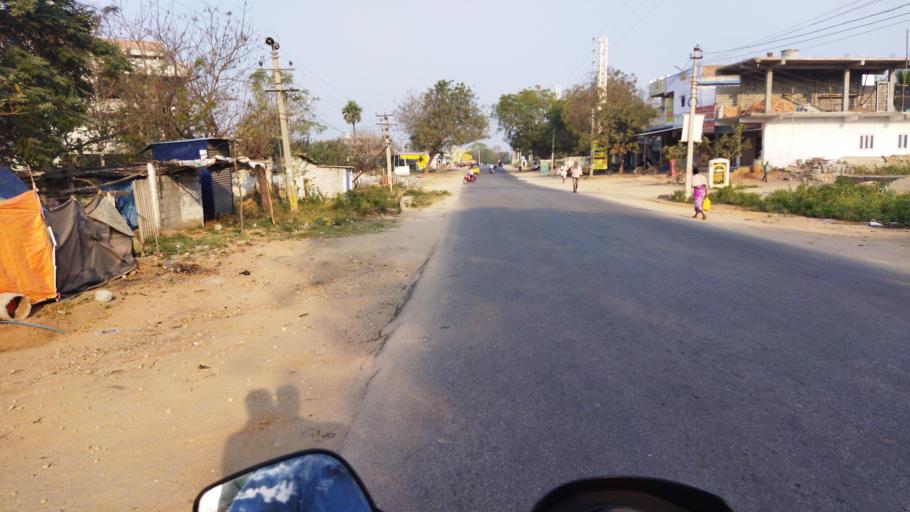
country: IN
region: Telangana
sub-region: Nalgonda
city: Nalgonda
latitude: 17.2352
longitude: 79.1227
